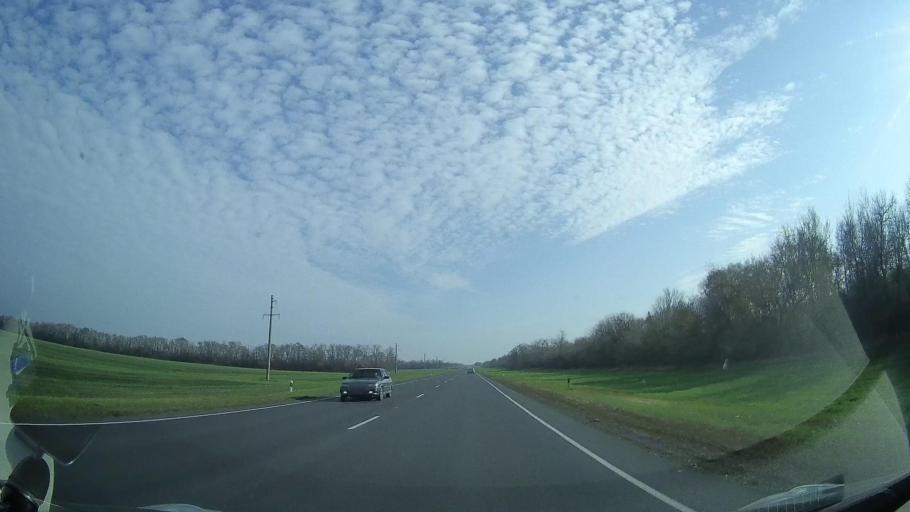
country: RU
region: Rostov
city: Gigant
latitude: 46.5279
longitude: 41.2058
